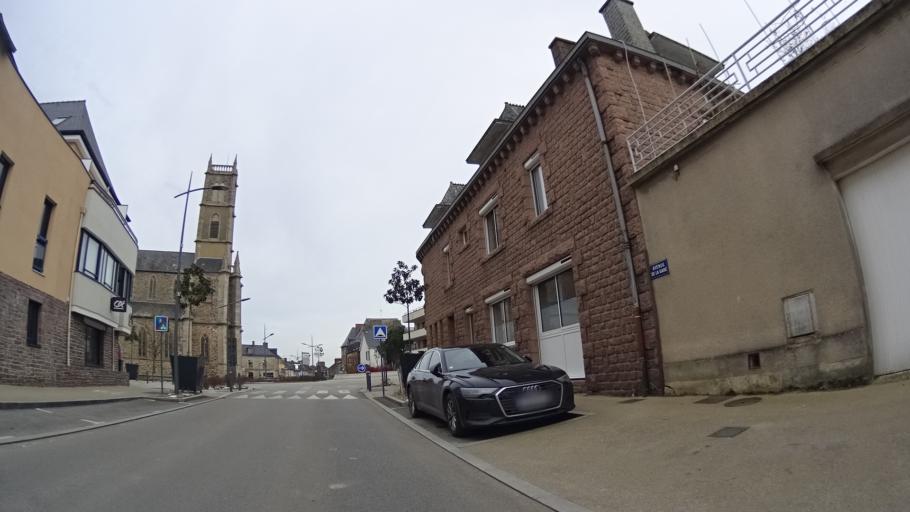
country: FR
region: Brittany
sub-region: Departement d'Ille-et-Vilaine
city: Montauban-de-Bretagne
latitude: 48.1985
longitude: -2.0478
